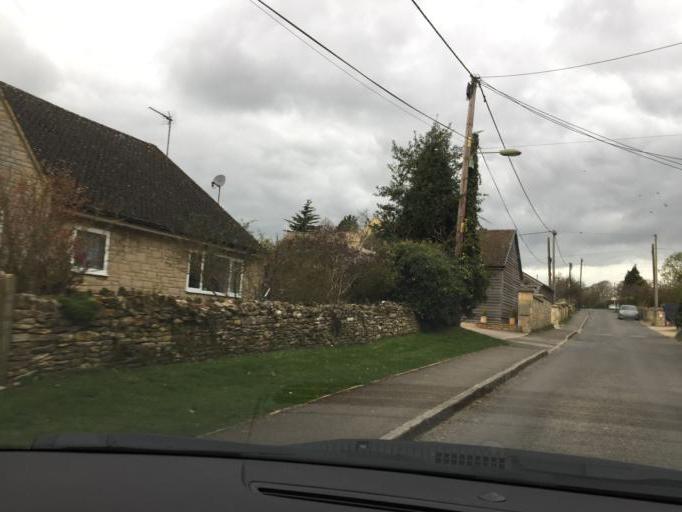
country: GB
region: England
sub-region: Oxfordshire
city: Chipping Norton
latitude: 51.9531
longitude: -1.5427
